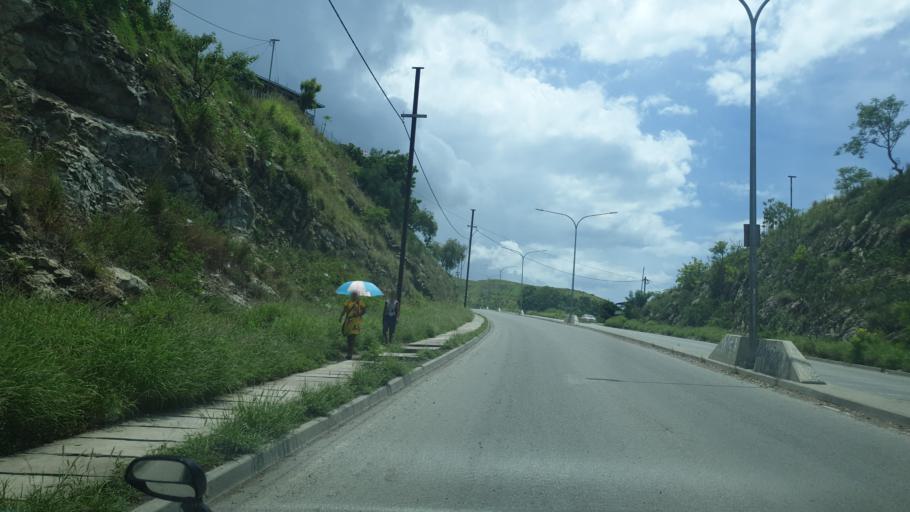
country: PG
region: National Capital
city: Port Moresby
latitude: -9.4515
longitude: 147.1542
